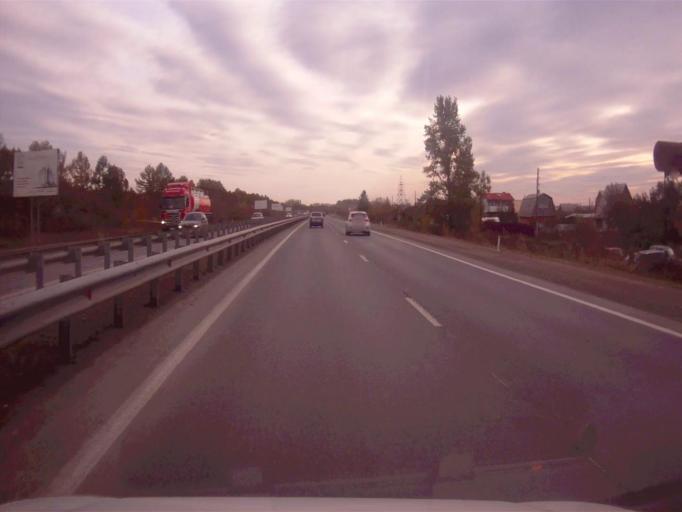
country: RU
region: Chelyabinsk
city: Novosineglazovskiy
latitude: 55.0264
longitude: 61.4501
